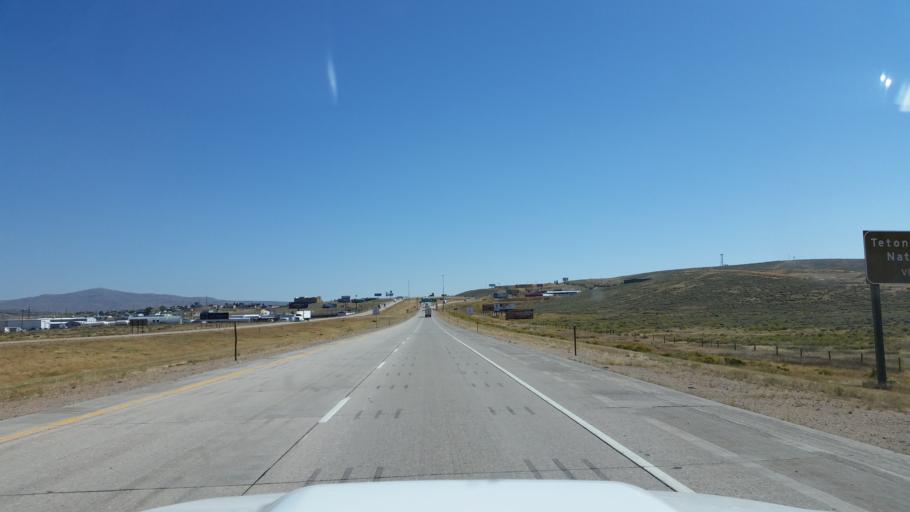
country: US
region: Wyoming
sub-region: Uinta County
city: Evanston
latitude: 41.2538
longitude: -111.0003
